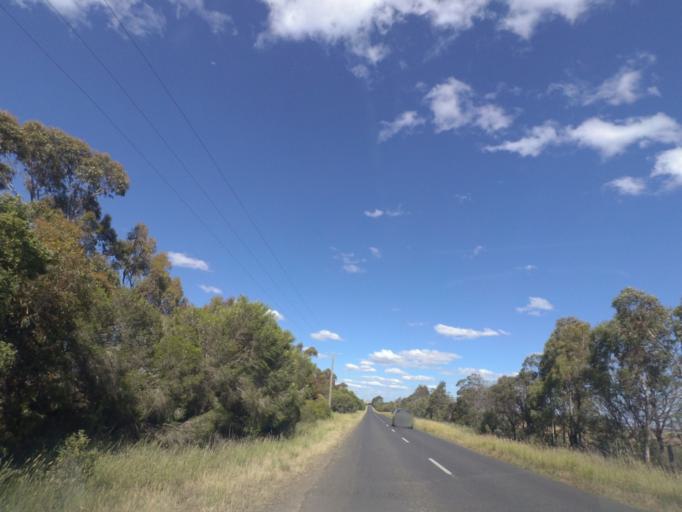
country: AU
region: Victoria
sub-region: Hume
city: Sunbury
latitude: -37.4380
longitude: 144.8164
